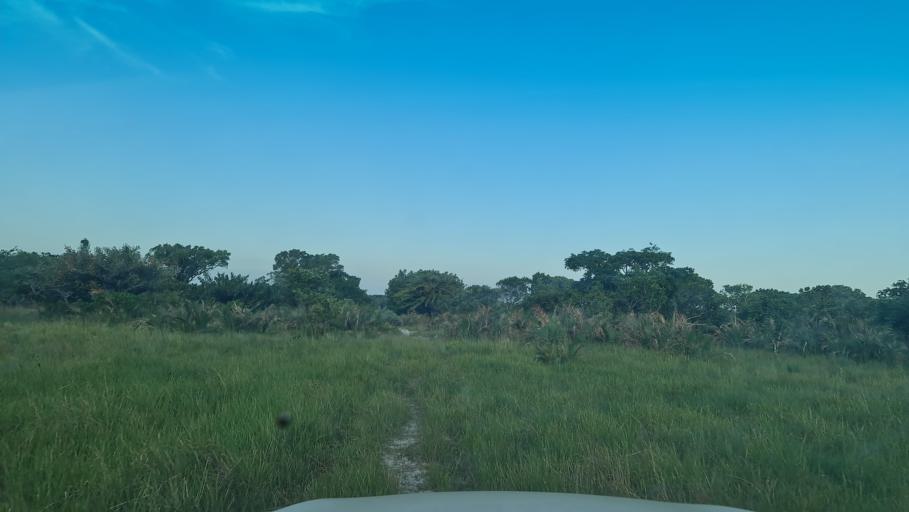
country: MZ
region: Gaza
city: Macia
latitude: -25.2135
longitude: 33.0545
